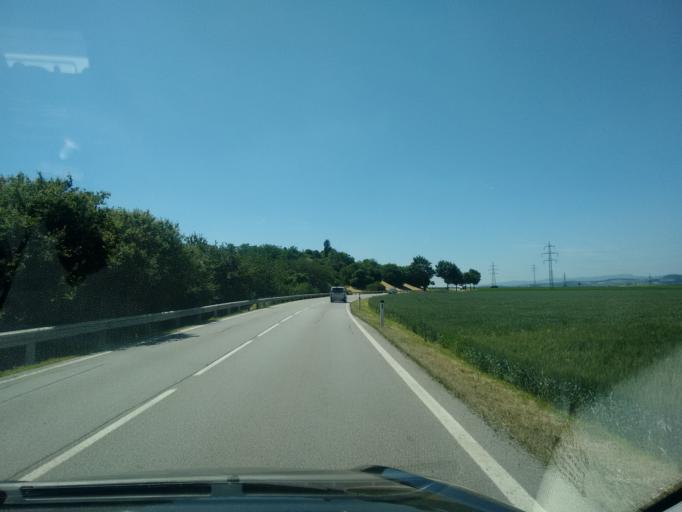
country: AT
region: Lower Austria
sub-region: Sankt Polten Stadt
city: Sankt Poelten
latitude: 48.1988
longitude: 15.5977
